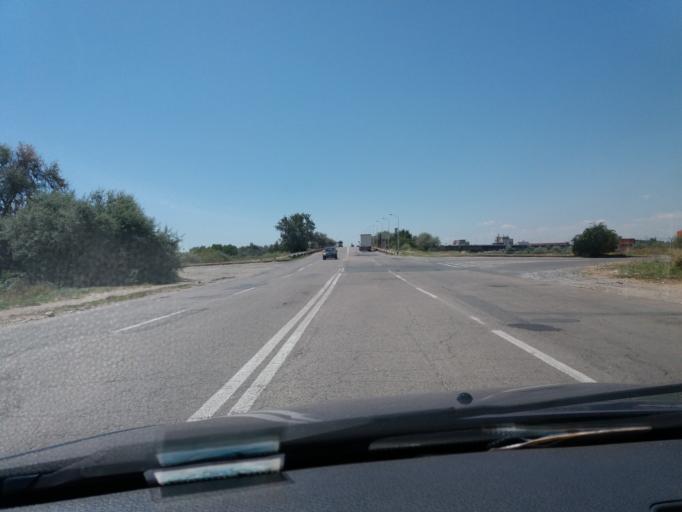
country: RO
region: Constanta
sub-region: Comuna Navodari
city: Navodari
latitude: 44.3259
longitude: 28.6252
